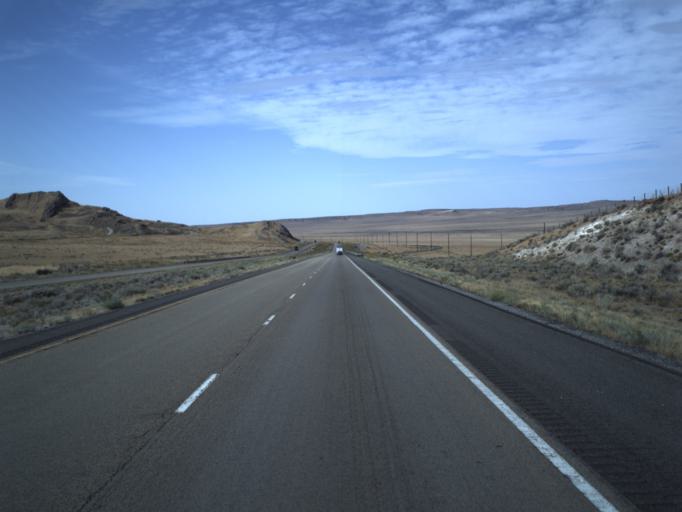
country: US
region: Utah
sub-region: Tooele County
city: Grantsville
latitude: 40.8188
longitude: -112.9110
